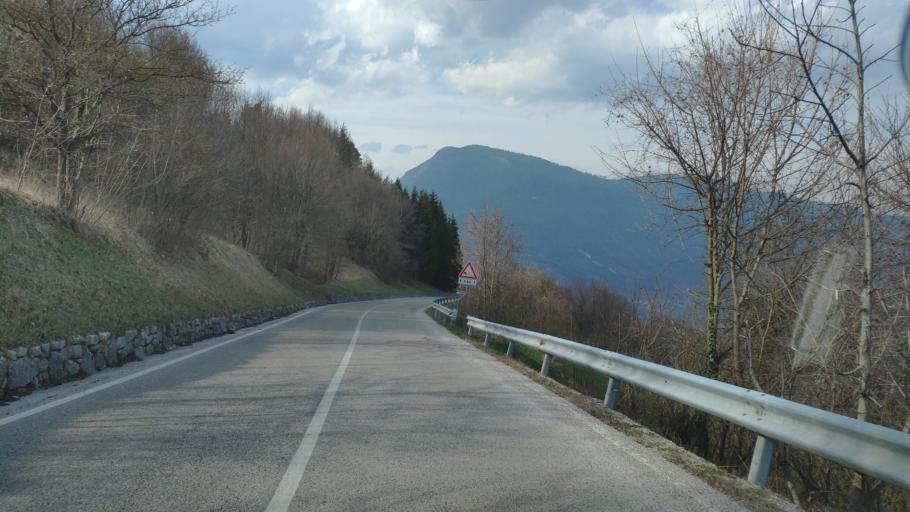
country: IT
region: Veneto
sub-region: Provincia di Vicenza
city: Enego
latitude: 45.9450
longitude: 11.7139
